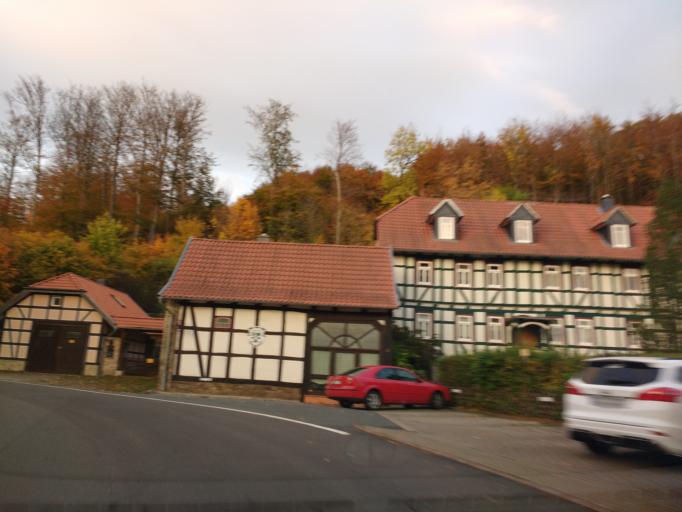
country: DE
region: Thuringia
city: Kleinbartloff
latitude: 51.3489
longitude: 10.3617
